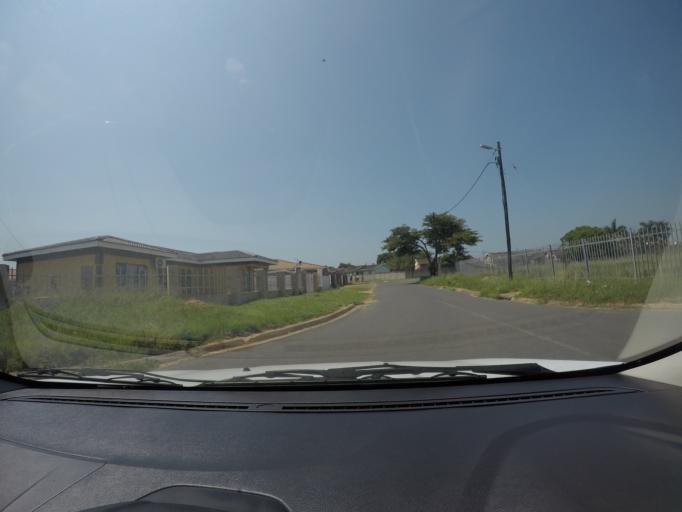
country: ZA
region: KwaZulu-Natal
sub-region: uThungulu District Municipality
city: eSikhawini
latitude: -28.8647
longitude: 31.9243
